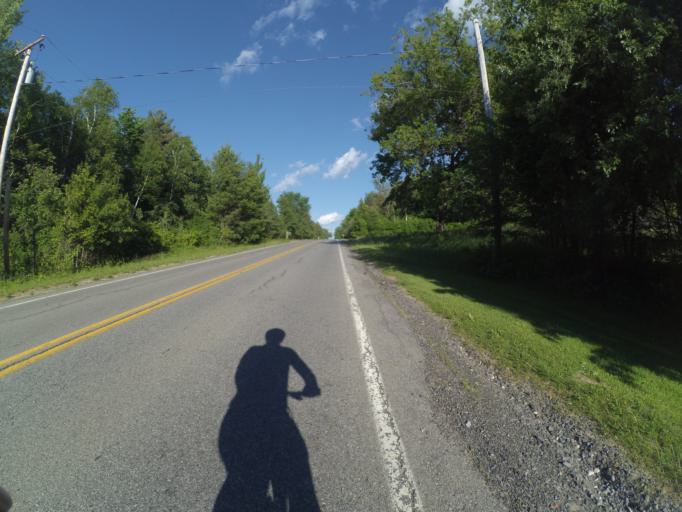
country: US
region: New York
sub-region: St. Lawrence County
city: Norwood
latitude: 44.7691
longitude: -74.9162
